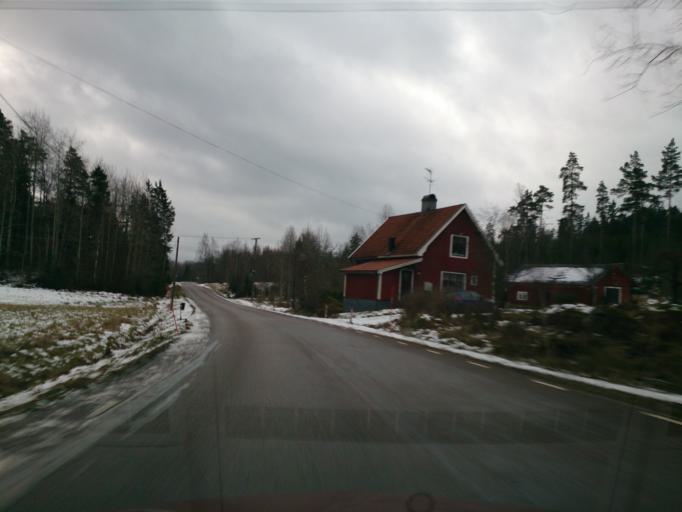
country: SE
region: OEstergoetland
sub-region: Atvidabergs Kommun
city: Atvidaberg
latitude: 58.2736
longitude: 16.0313
